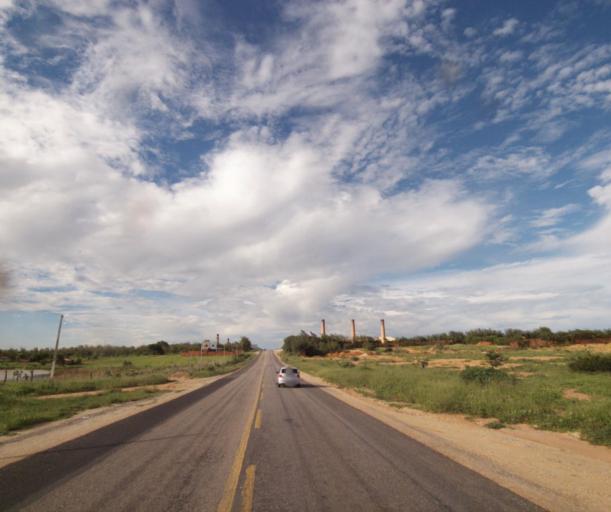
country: BR
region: Bahia
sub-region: Guanambi
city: Guanambi
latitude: -14.2659
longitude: -42.7827
